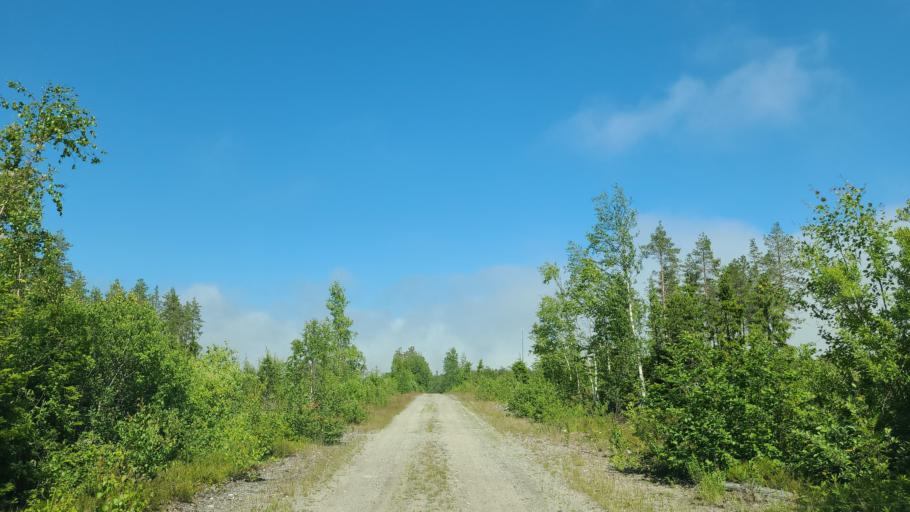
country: SE
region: Vaesternorrland
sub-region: OErnskoeldsviks Kommun
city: Husum
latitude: 63.4420
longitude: 19.2345
